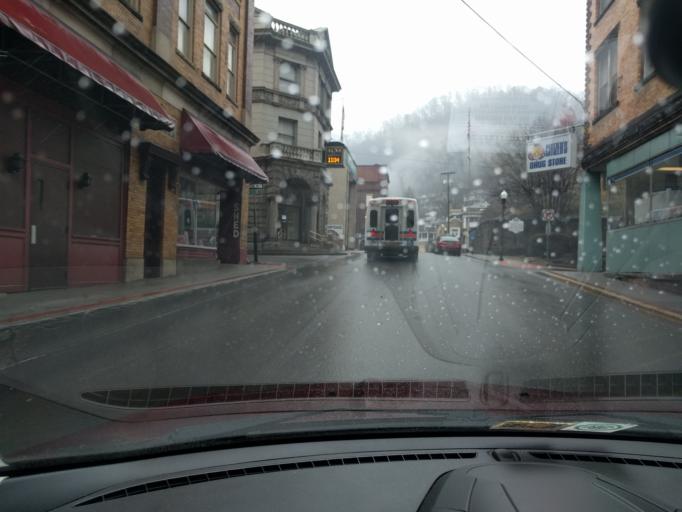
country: US
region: West Virginia
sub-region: McDowell County
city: Welch
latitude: 37.4320
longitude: -81.5846
